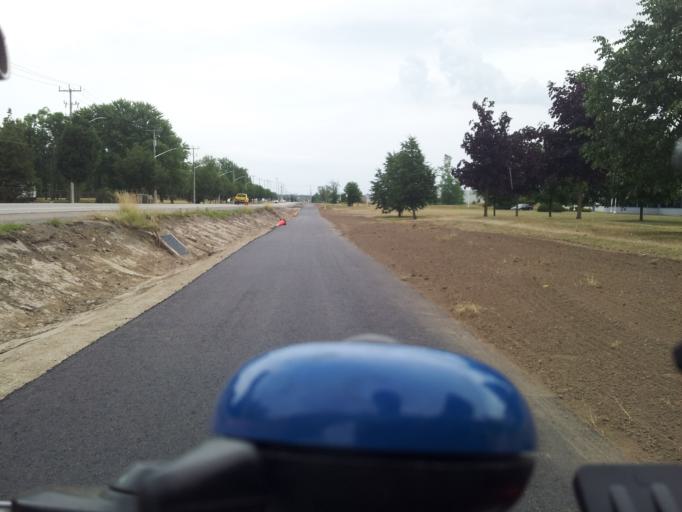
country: CA
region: Ontario
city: Stratford
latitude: 43.3602
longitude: -81.0059
